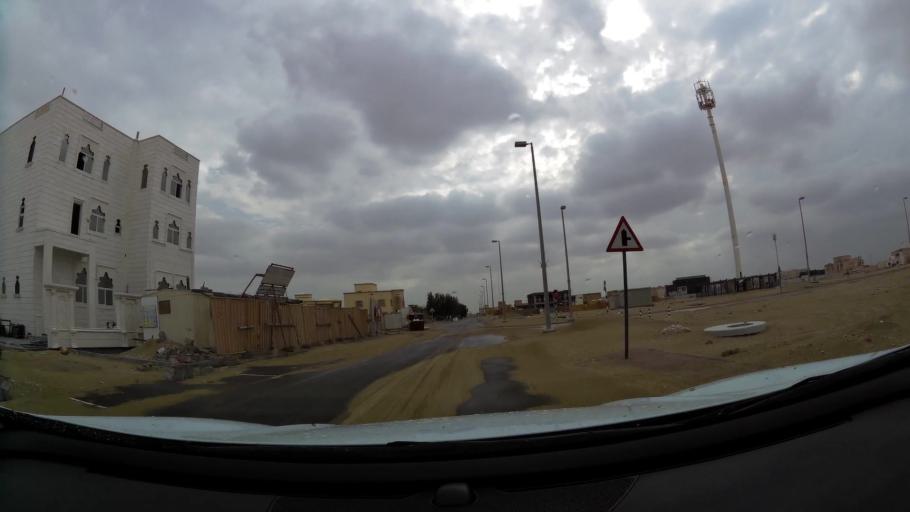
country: AE
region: Abu Dhabi
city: Abu Dhabi
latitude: 24.3593
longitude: 54.6204
